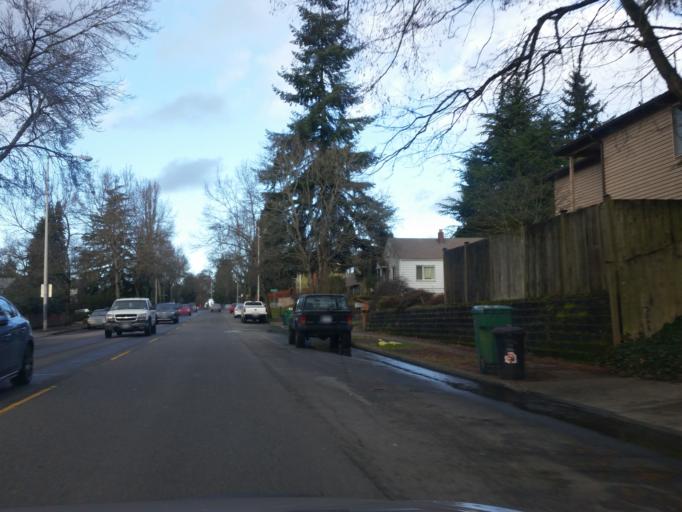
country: US
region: Washington
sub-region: King County
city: Lake Forest Park
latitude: 47.7243
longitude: -122.2909
